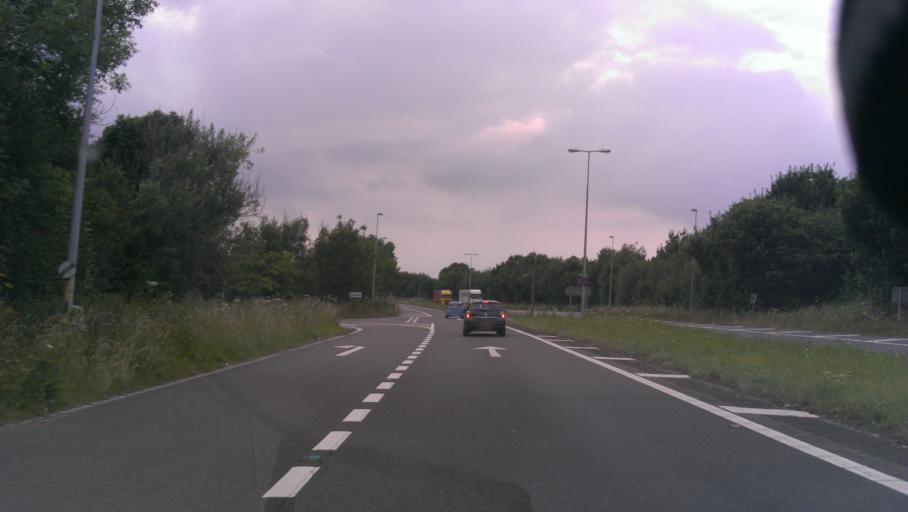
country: GB
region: England
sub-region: Kent
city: Shepherdswell
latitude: 51.1716
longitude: 1.2456
